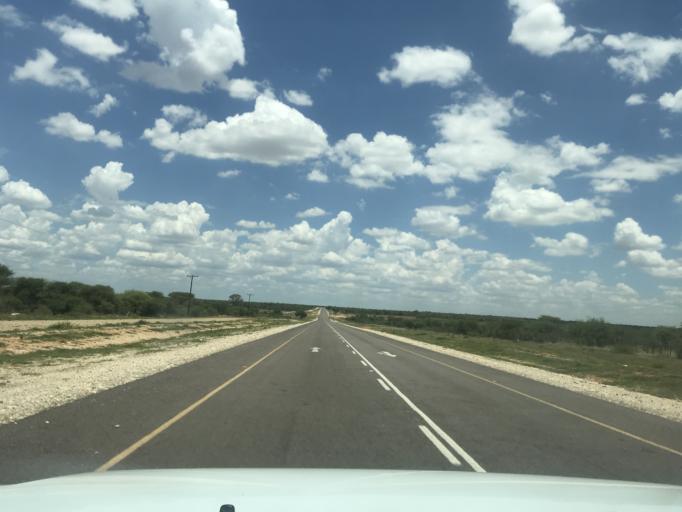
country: BW
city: Mabuli
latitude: -25.7140
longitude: 25.0622
